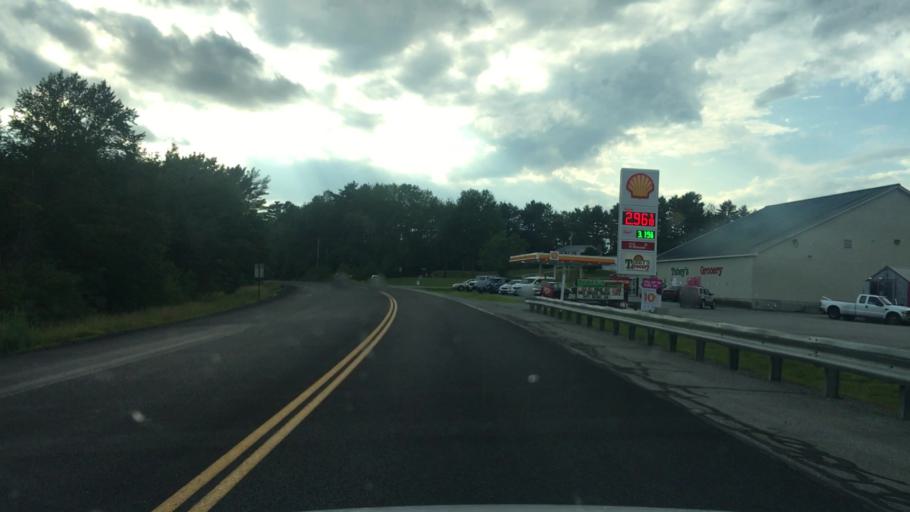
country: US
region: Maine
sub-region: Waldo County
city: Palermo
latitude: 44.4106
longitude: -69.4846
